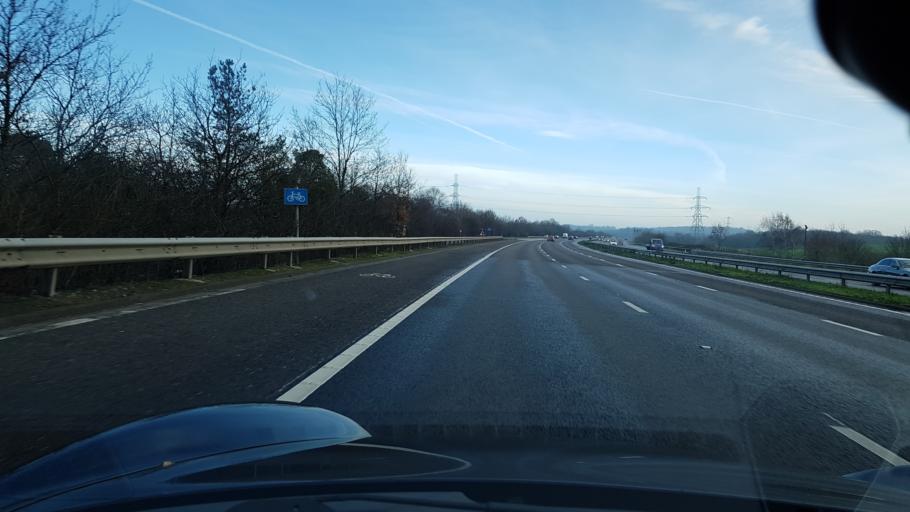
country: GB
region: England
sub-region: Surrey
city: Esher
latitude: 51.3494
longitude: -0.3604
